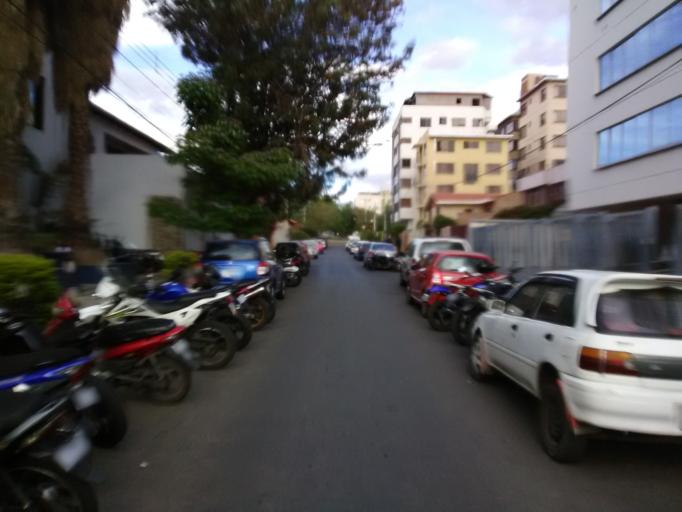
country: BO
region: Cochabamba
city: Cochabamba
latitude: -17.3697
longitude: -66.1603
